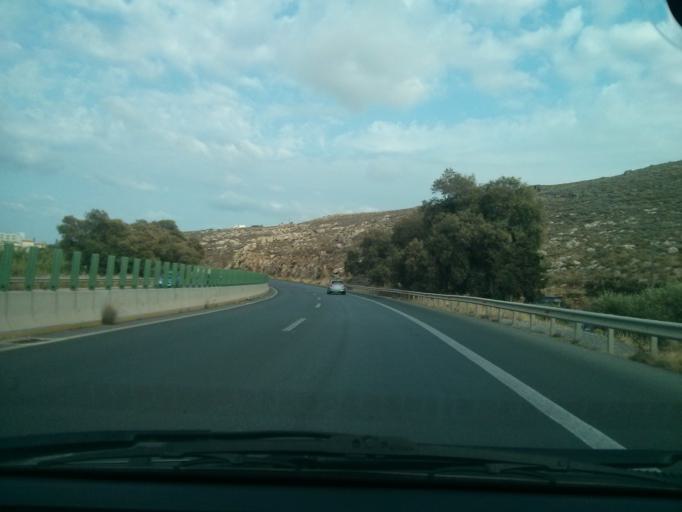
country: GR
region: Crete
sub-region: Nomos Irakleiou
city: Kokkini Hani
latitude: 35.3288
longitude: 25.2366
